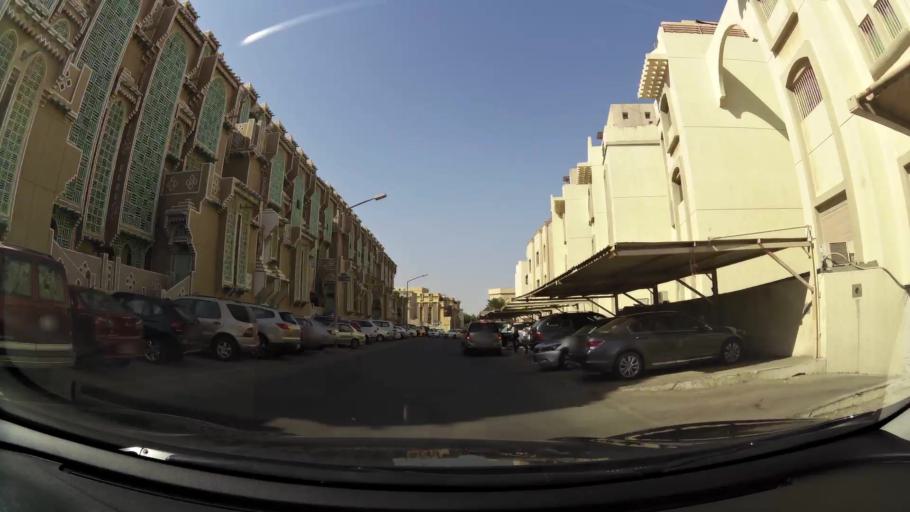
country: KW
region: Muhafazat Hawalli
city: Salwa
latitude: 29.2869
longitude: 48.0754
